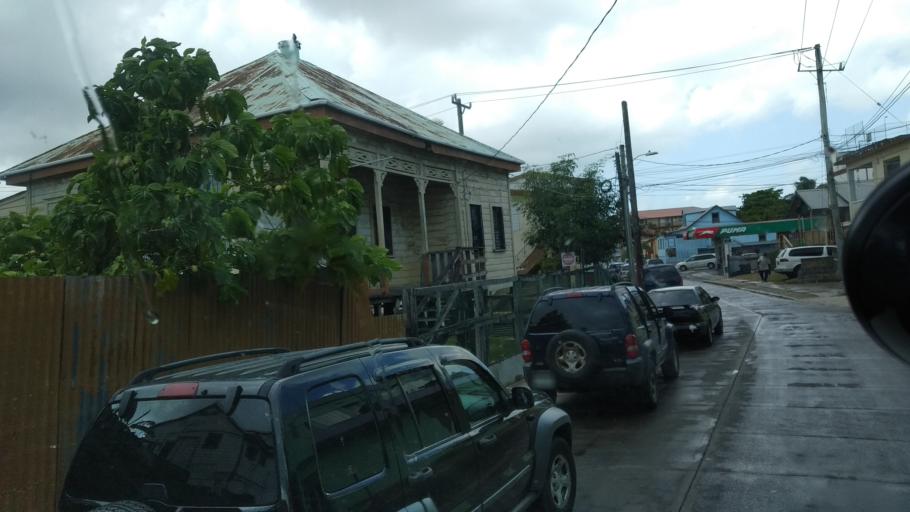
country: BZ
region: Belize
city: Belize City
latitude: 17.4998
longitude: -88.1889
